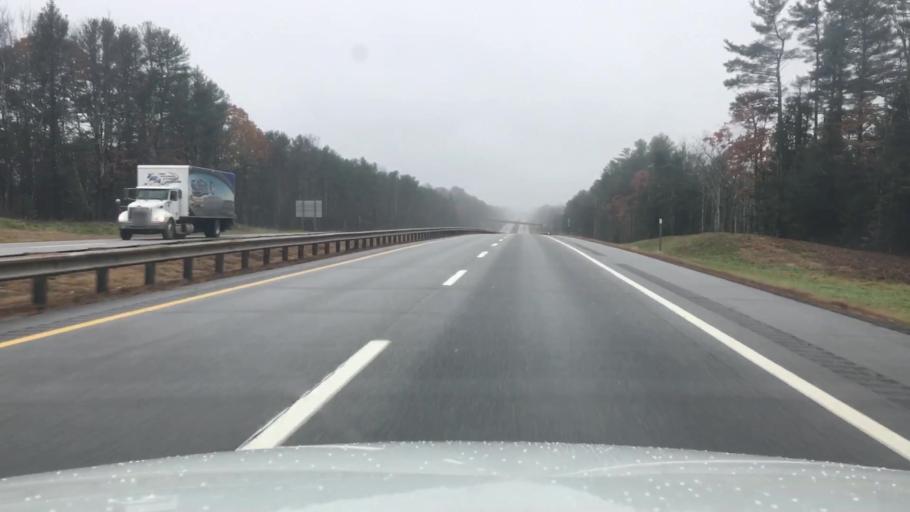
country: US
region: Maine
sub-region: Sagadahoc County
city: Richmond
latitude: 44.1593
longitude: -69.8921
